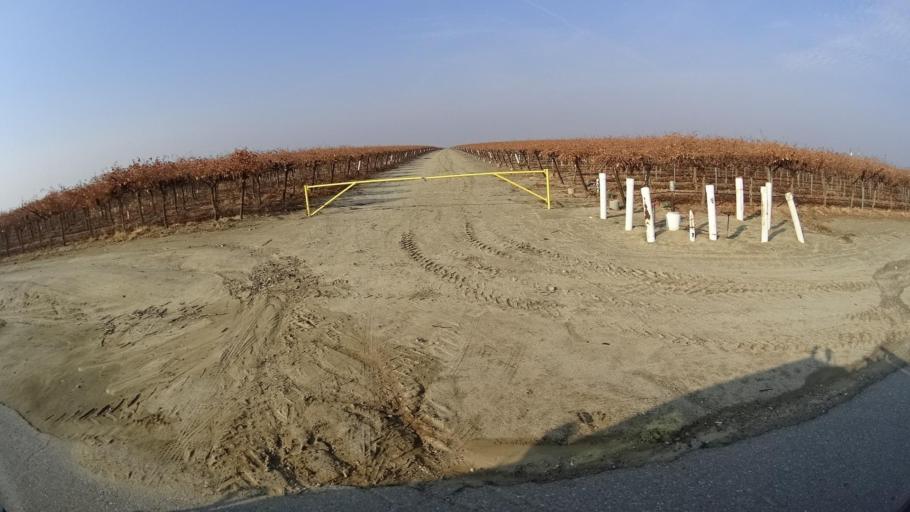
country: US
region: California
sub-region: Kern County
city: Arvin
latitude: 35.0655
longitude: -118.9175
